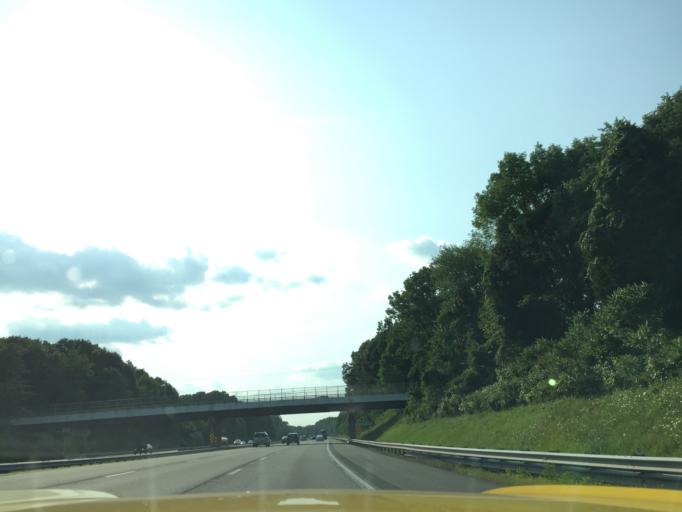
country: US
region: Maryland
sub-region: Cecil County
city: North East
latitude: 39.6419
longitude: -75.9097
